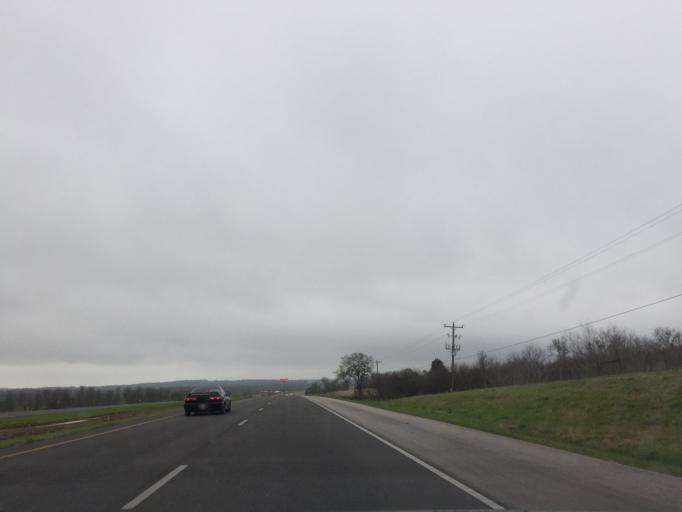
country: US
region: Texas
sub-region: Travis County
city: Garfield
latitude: 30.1724
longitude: -97.5219
